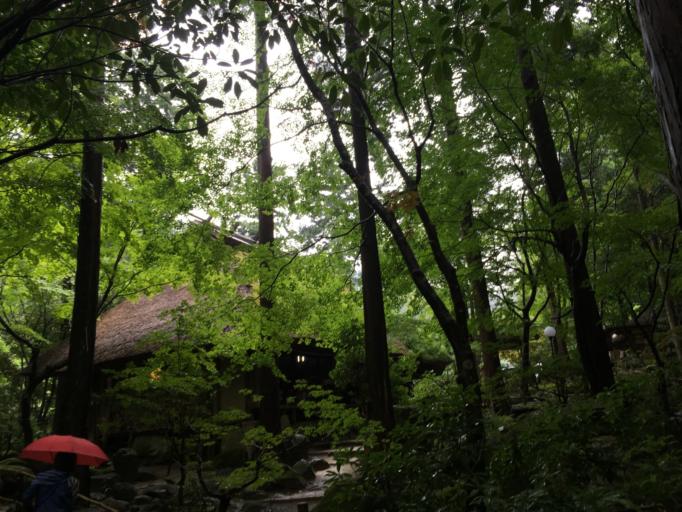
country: JP
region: Tottori
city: Tottori
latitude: 35.2898
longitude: 134.3124
